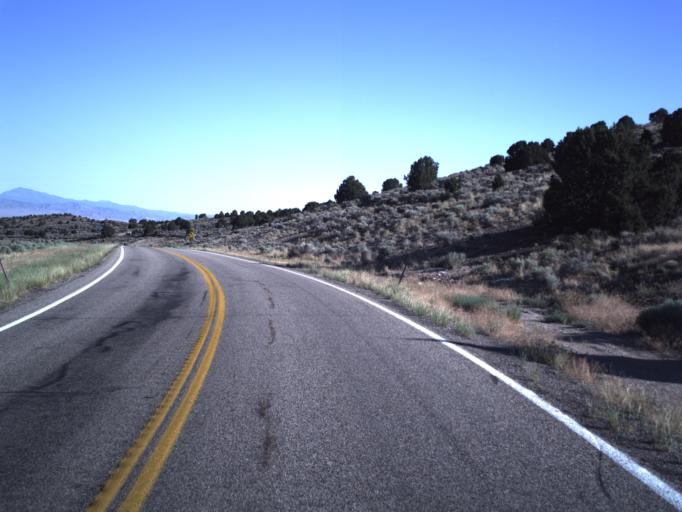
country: US
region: Utah
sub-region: Iron County
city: Parowan
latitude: 38.1086
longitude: -112.9466
